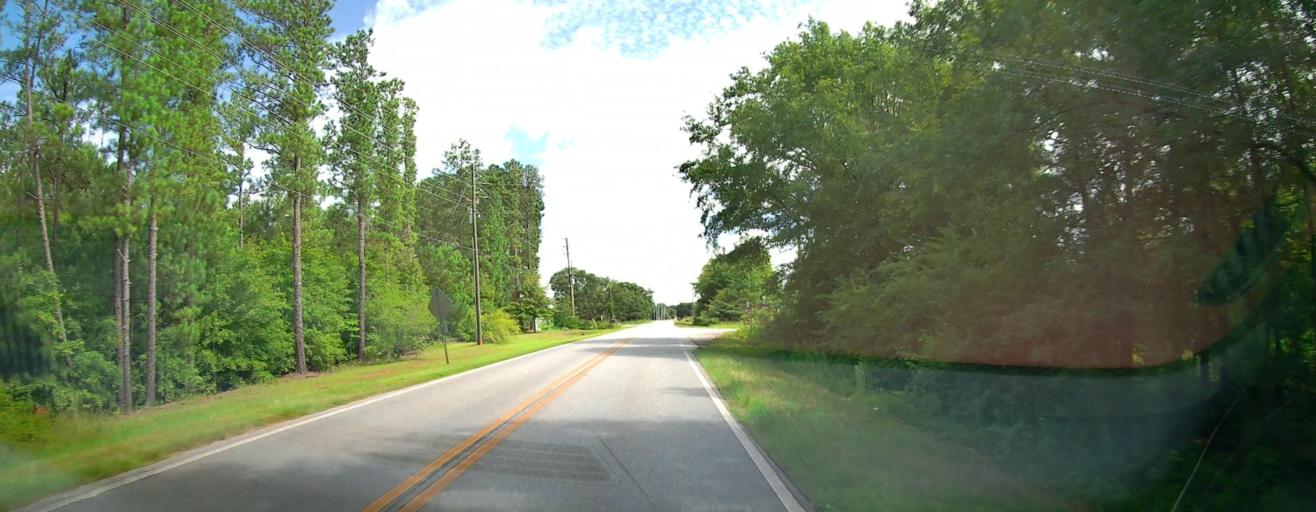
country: US
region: Georgia
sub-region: Peach County
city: Byron
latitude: 32.6219
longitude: -83.7995
